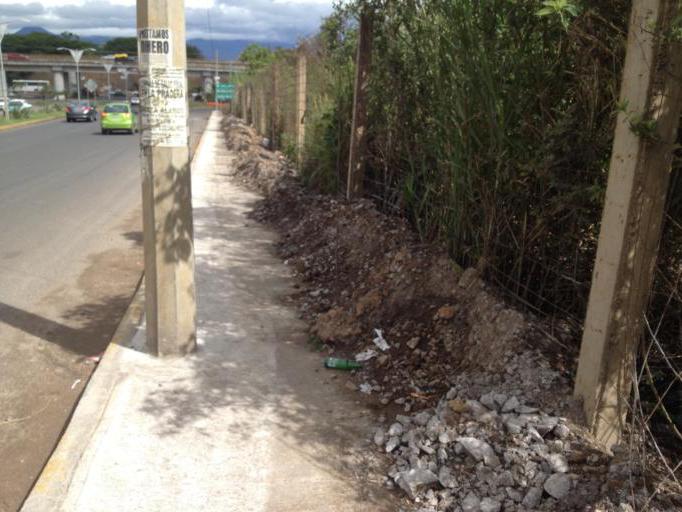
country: MX
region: Veracruz
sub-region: Emiliano Zapata
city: Las Trancas
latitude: 19.5063
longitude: -96.8560
